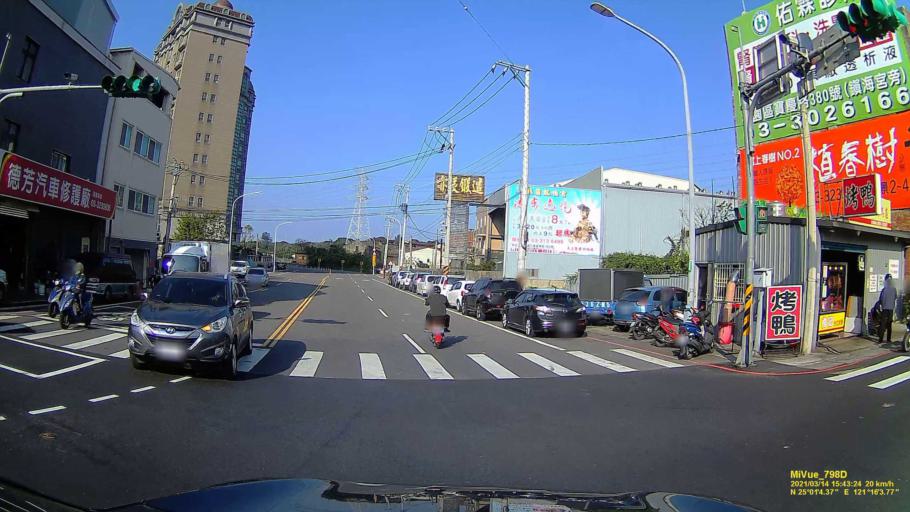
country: TW
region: Taiwan
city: Taoyuan City
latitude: 25.0180
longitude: 121.2678
